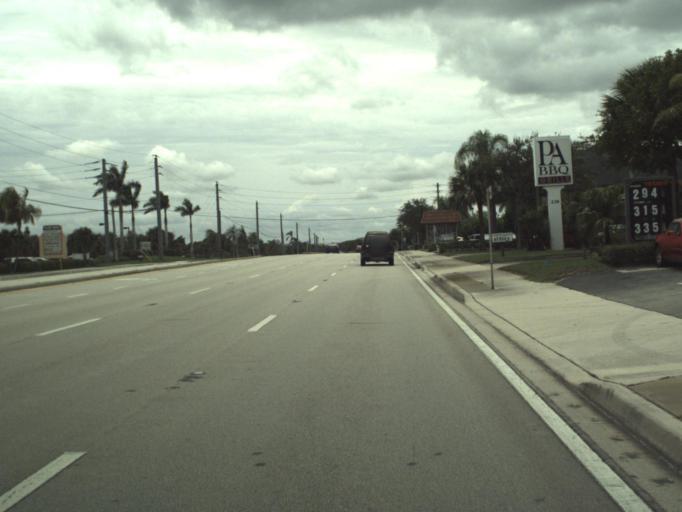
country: US
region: Florida
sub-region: Palm Beach County
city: Jupiter
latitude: 26.9576
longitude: -80.0850
